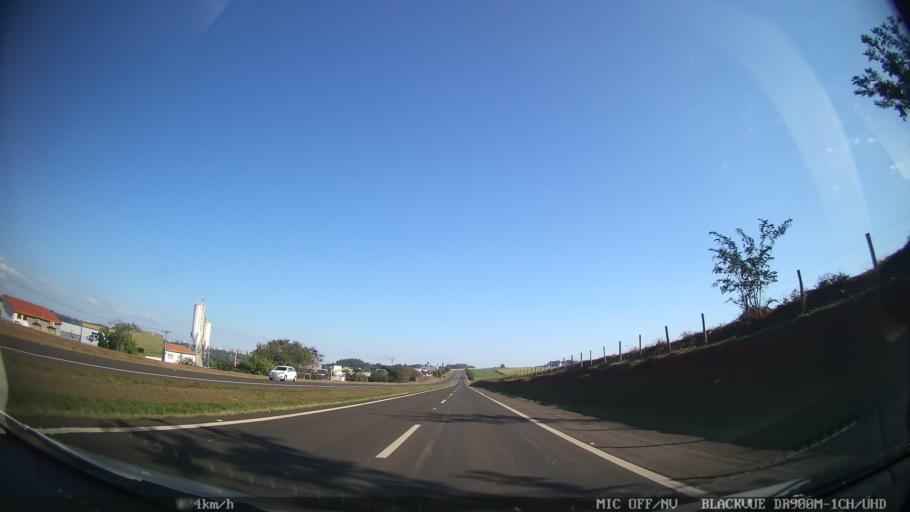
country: BR
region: Sao Paulo
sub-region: Piracicaba
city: Piracicaba
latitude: -22.6788
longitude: -47.6348
